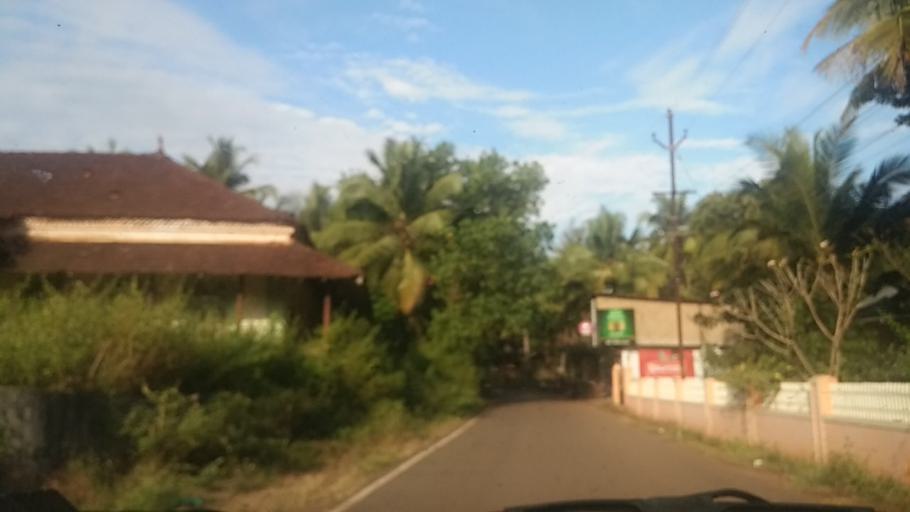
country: IN
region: Goa
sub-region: South Goa
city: Cuncolim
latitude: 15.1808
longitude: 73.9699
